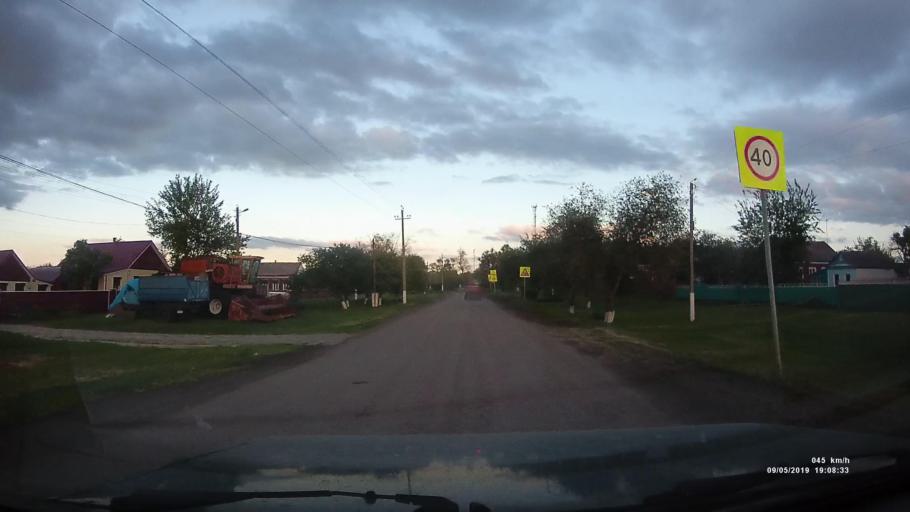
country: RU
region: Krasnodarskiy
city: Kanelovskaya
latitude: 46.7292
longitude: 39.2047
